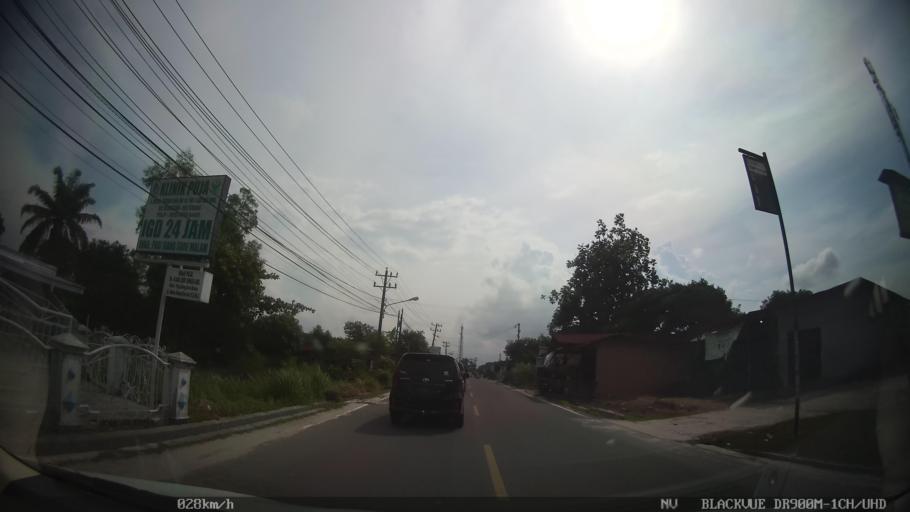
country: ID
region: North Sumatra
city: Percut
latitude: 3.6089
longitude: 98.7971
